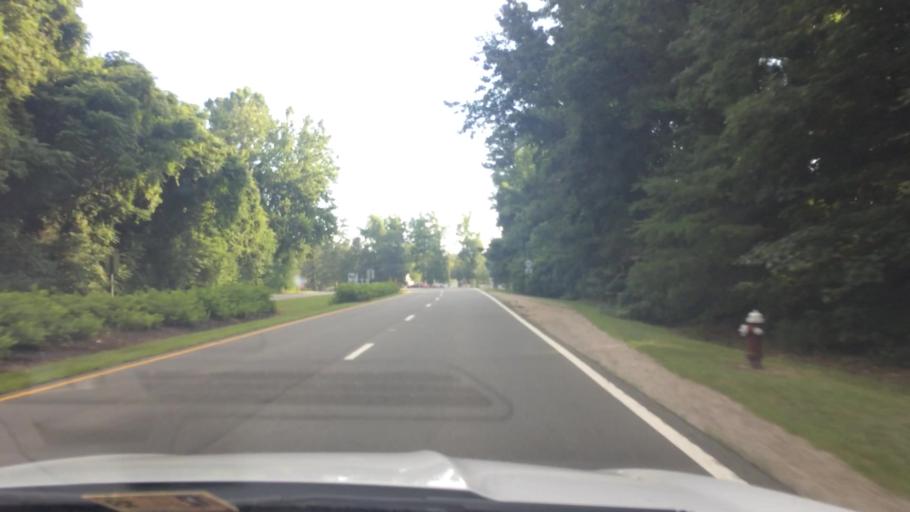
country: US
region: Virginia
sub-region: City of Williamsburg
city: Williamsburg
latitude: 37.2663
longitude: -76.6395
